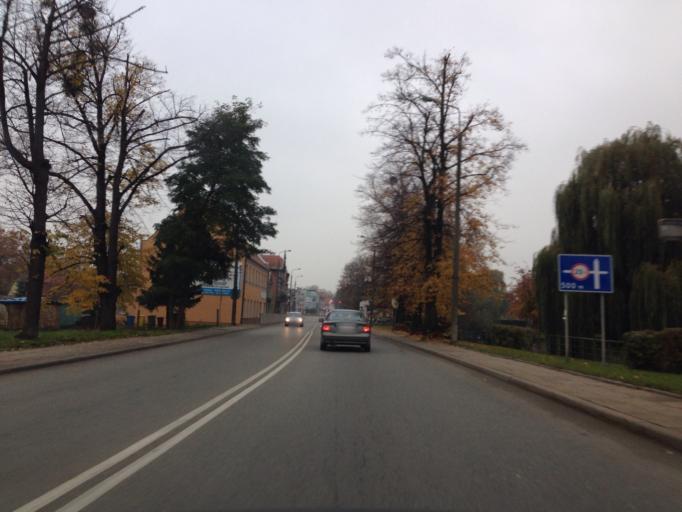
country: PL
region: Pomeranian Voivodeship
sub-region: Powiat gdanski
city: Pruszcz Gdanski
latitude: 54.2649
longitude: 18.6360
